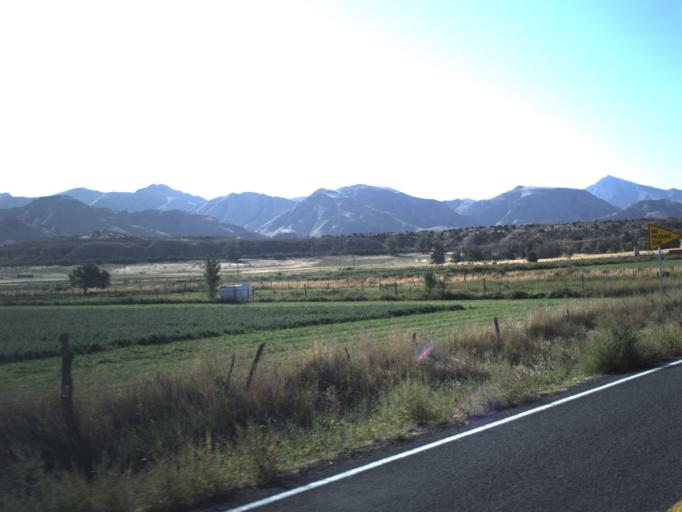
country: US
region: Utah
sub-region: Millard County
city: Delta
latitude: 39.5298
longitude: -112.2734
